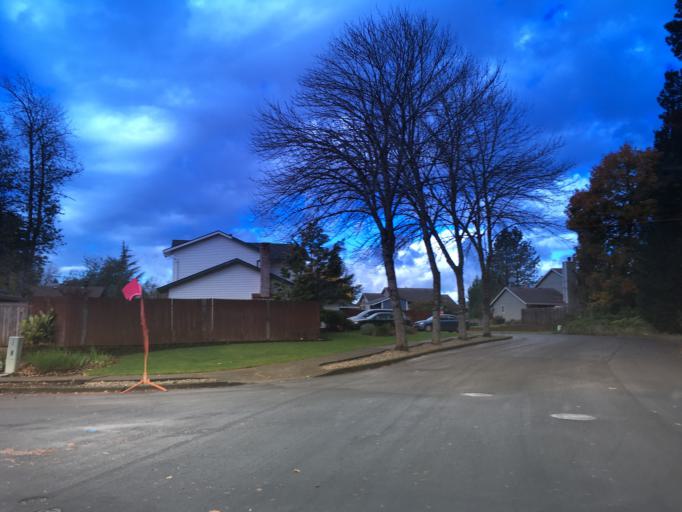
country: US
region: Oregon
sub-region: Multnomah County
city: Troutdale
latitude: 45.5178
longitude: -122.3819
